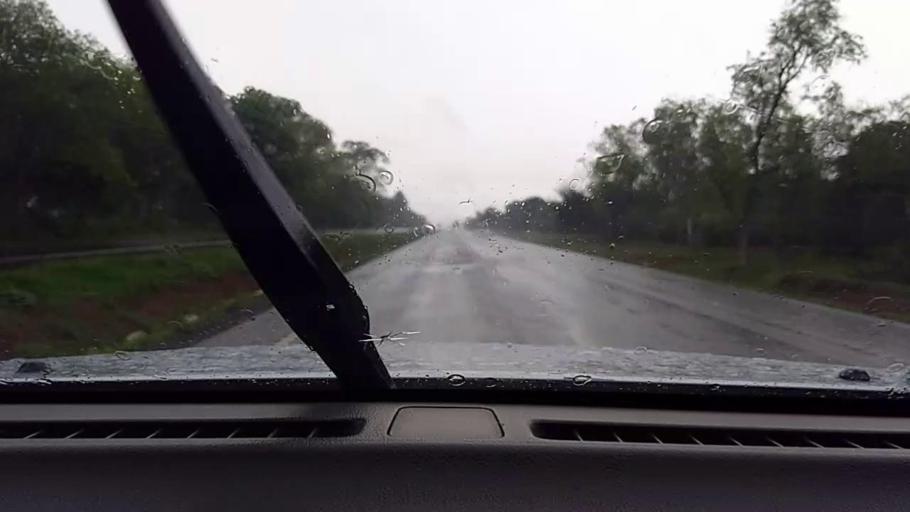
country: PY
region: Caaguazu
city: Repatriacion
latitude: -25.4502
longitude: -55.8992
